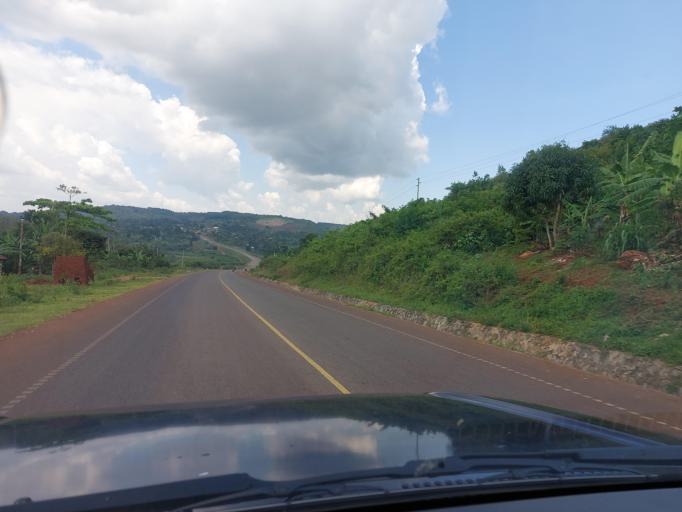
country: UG
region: Central Region
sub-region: Buikwe District
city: Njeru
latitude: 0.3367
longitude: 33.1251
